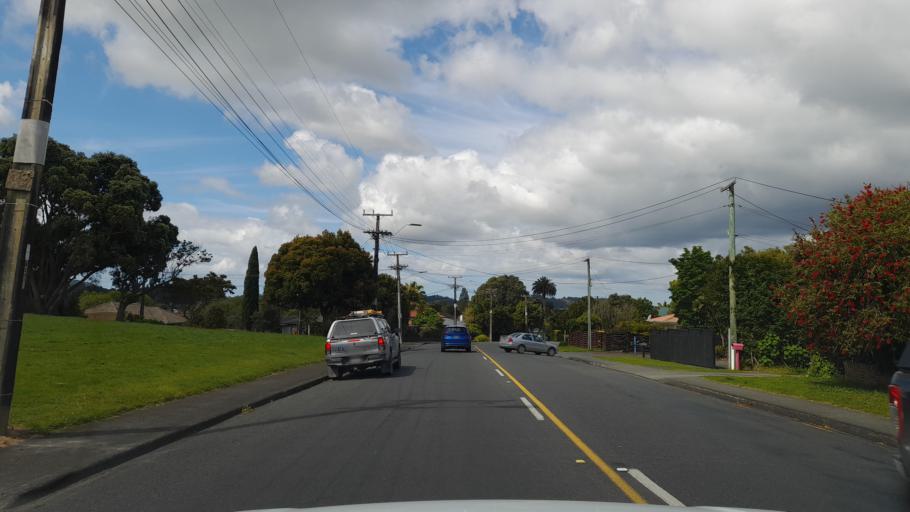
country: NZ
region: Northland
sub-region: Whangarei
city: Whangarei
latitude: -35.6969
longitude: 174.3061
